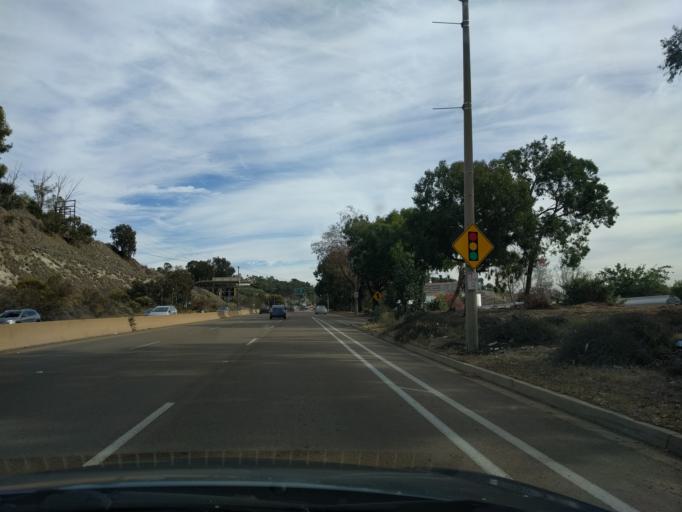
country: US
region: California
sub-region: San Diego County
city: San Diego
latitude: 32.7868
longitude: -117.1196
